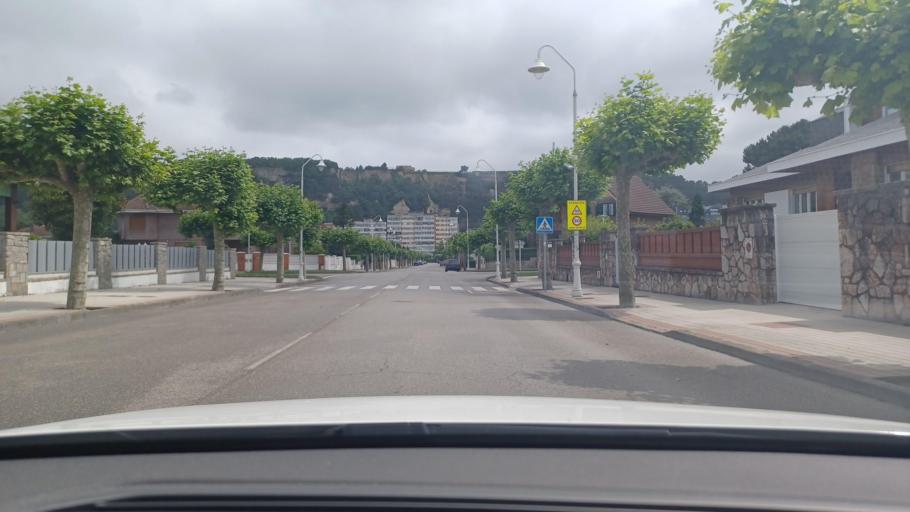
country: ES
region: Asturias
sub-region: Province of Asturias
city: Aviles
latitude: 43.5764
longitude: -5.9545
